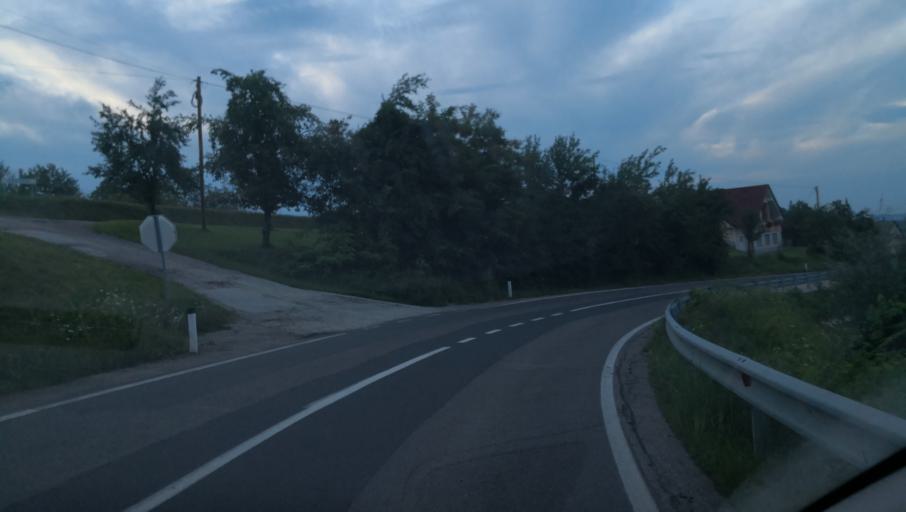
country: SI
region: Metlika
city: Metlika
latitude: 45.6912
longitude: 15.2648
